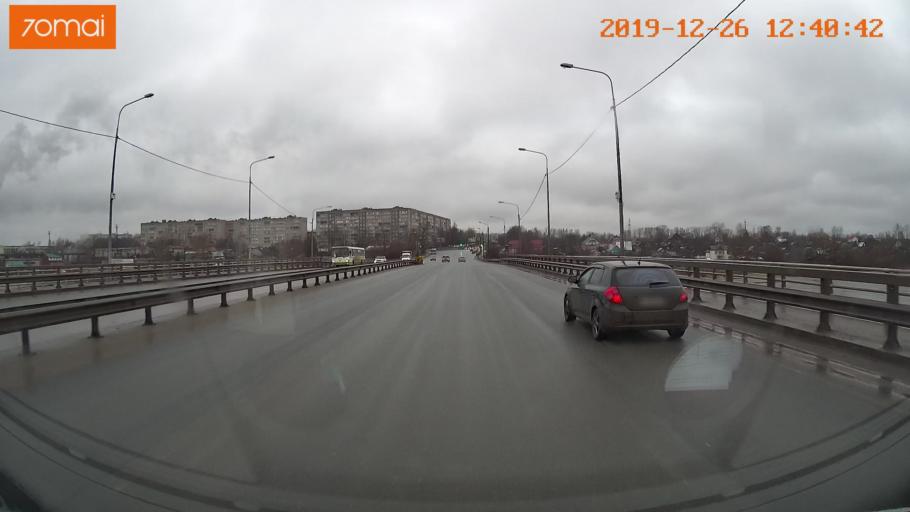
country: RU
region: Vologda
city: Tonshalovo
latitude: 59.1434
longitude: 37.9696
